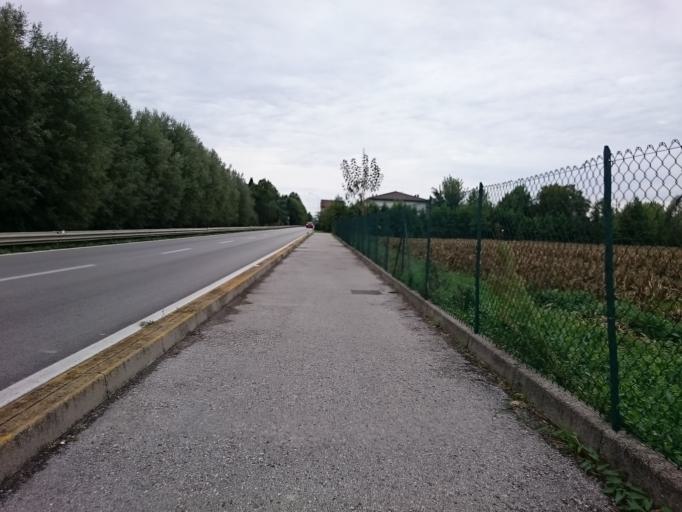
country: IT
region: Veneto
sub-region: Provincia di Vicenza
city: Quinto Vicentino
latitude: 45.5659
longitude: 11.6465
